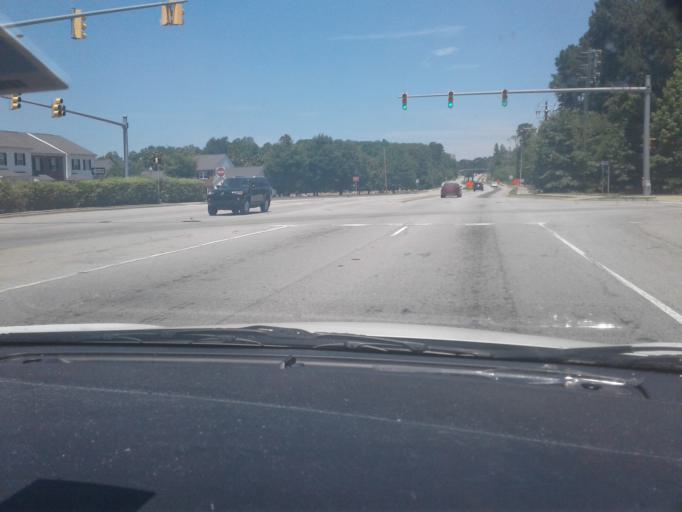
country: US
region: North Carolina
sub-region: Wake County
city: Fuquay-Varina
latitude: 35.6046
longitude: -78.8043
